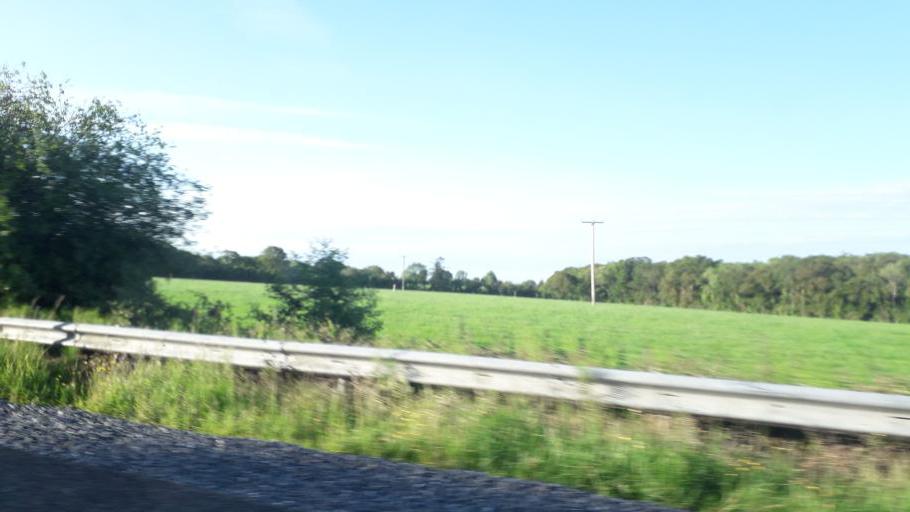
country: IE
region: Leinster
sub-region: Loch Garman
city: Loch Garman
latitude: 52.3609
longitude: -6.5093
